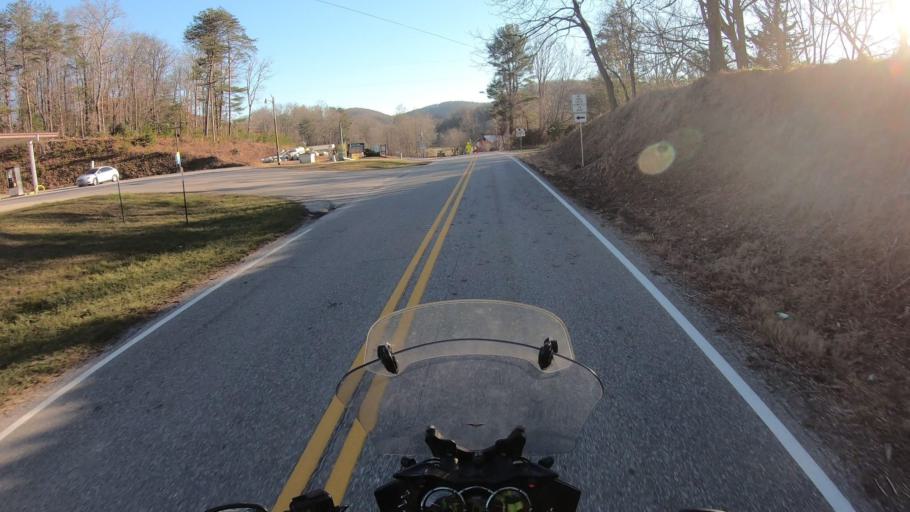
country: US
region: Georgia
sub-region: Lumpkin County
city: Dahlonega
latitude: 34.6967
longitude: -84.0305
